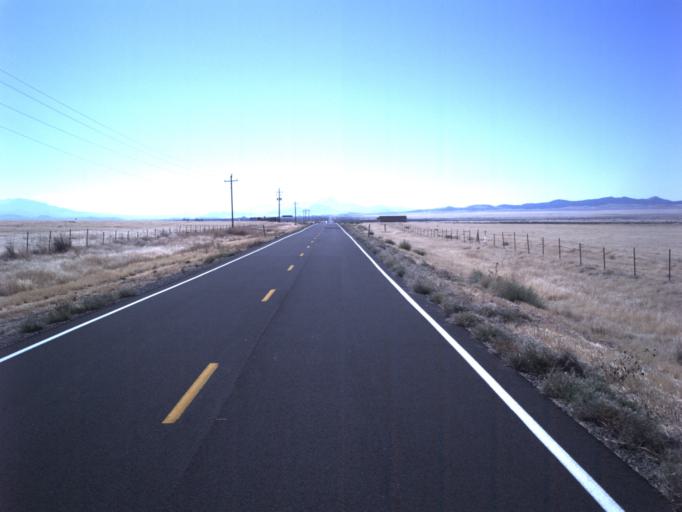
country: US
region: Utah
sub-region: Tooele County
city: Grantsville
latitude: 40.3888
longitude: -112.7473
